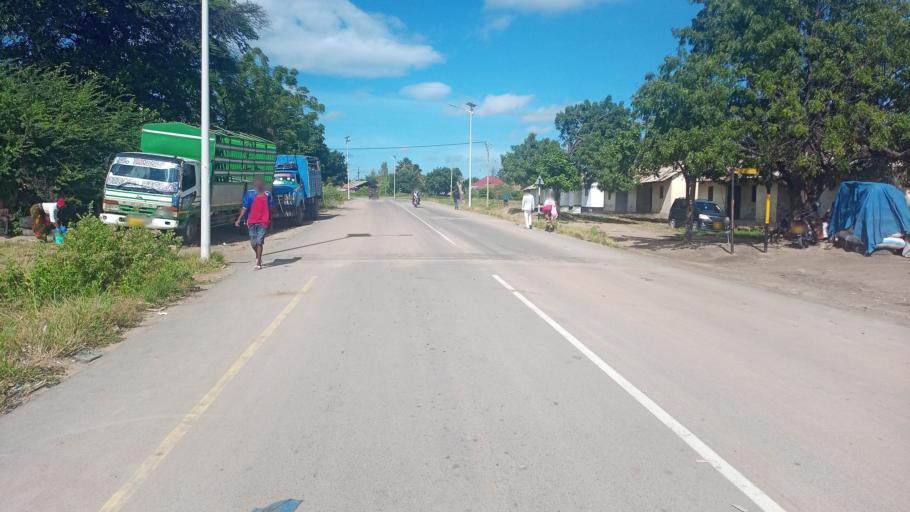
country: TZ
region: Dodoma
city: Dodoma
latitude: -6.1809
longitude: 35.7388
